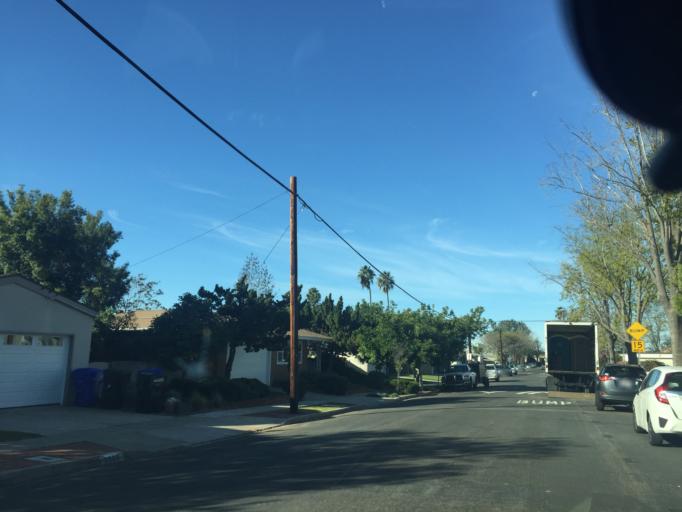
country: US
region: California
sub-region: San Diego County
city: La Mesa
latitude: 32.7736
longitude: -117.0815
